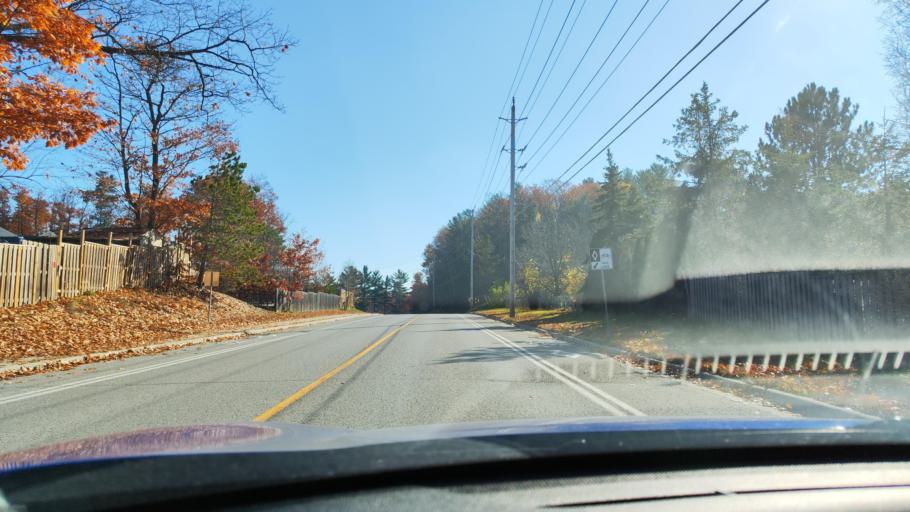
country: CA
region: Ontario
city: Wasaga Beach
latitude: 44.5204
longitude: -79.9967
